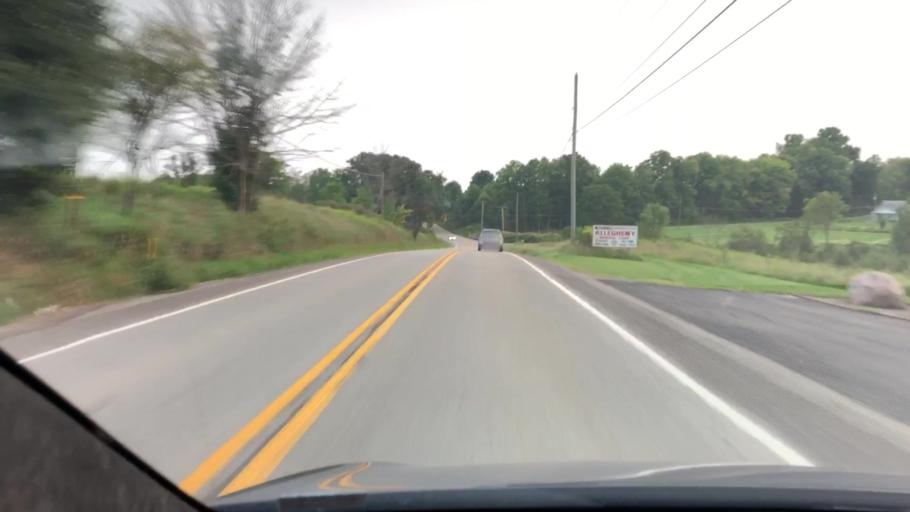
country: US
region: Pennsylvania
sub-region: Mercer County
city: Grove City
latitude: 41.1582
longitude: -80.0015
